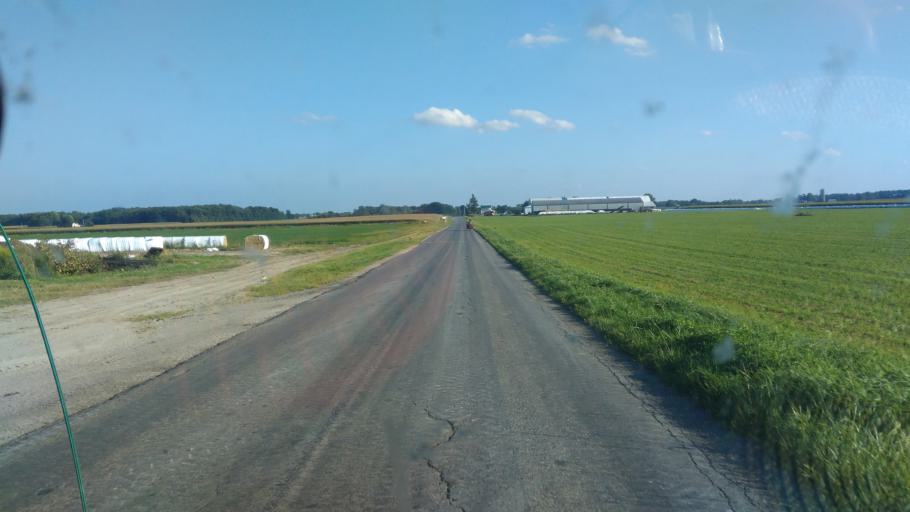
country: US
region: Ohio
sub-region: Huron County
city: Greenwich
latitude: 40.9480
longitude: -82.4563
